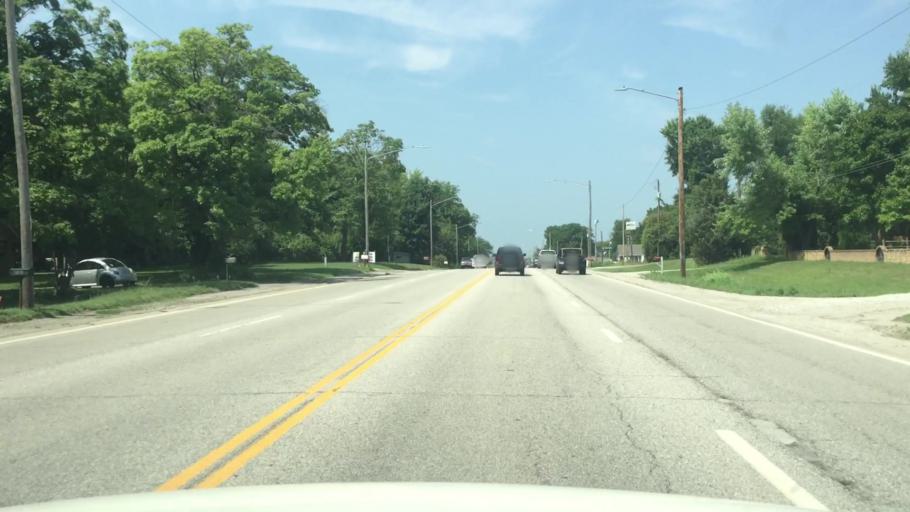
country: US
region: Kansas
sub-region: Crawford County
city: Frontenac
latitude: 37.4490
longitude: -94.7051
